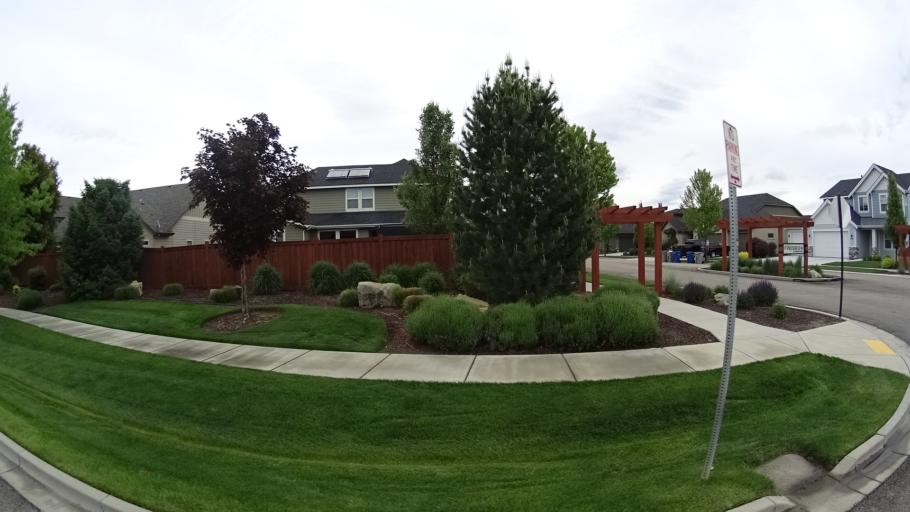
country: US
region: Idaho
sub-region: Ada County
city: Star
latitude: 43.6894
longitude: -116.4732
